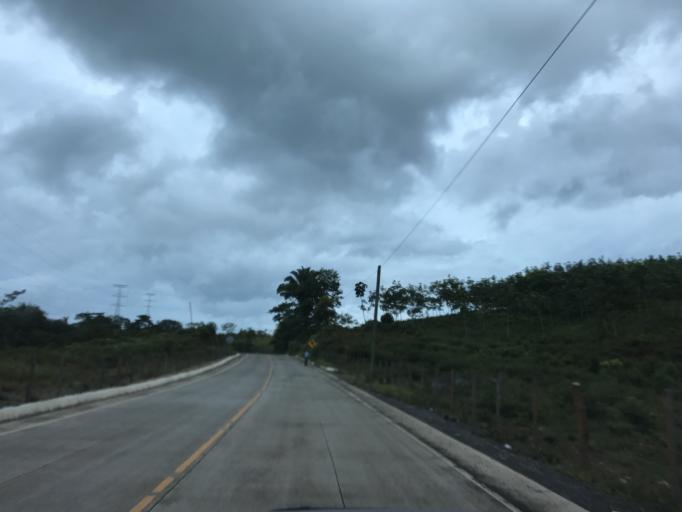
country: GT
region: Izabal
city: Morales
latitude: 15.6364
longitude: -89.0433
